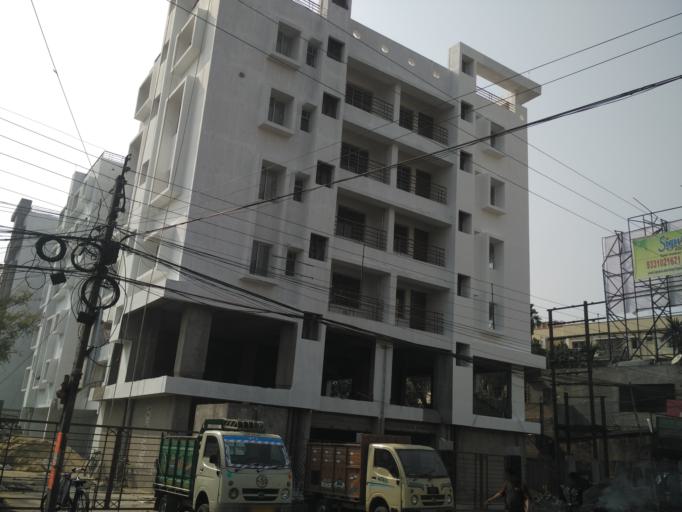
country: IN
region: West Bengal
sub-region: South 24 Paraganas
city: Baruipur
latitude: 22.4530
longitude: 88.3887
